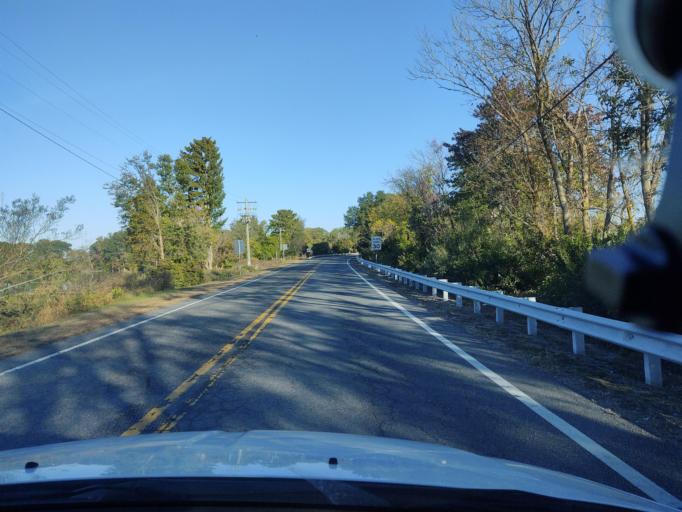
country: US
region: Maryland
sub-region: Queen Anne's County
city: Kingstown
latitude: 39.2430
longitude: -75.9236
